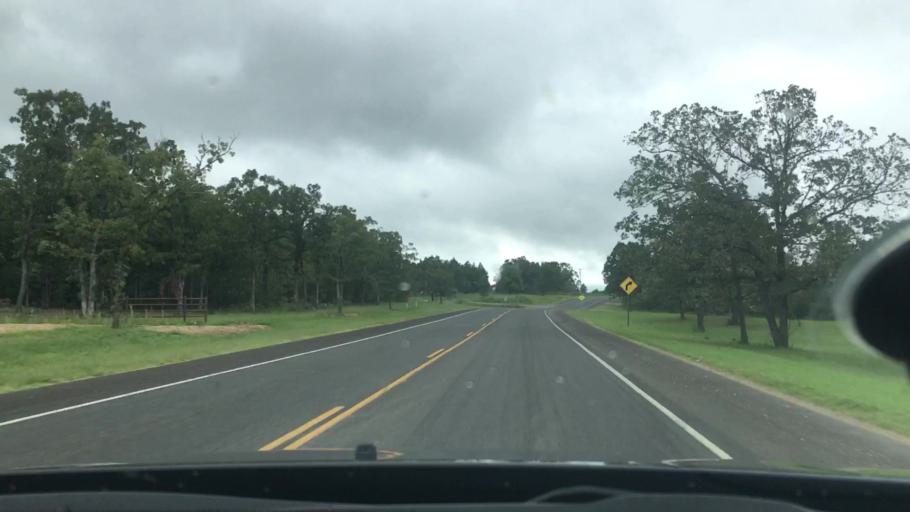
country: US
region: Oklahoma
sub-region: Sequoyah County
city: Vian
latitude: 35.5644
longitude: -94.9837
